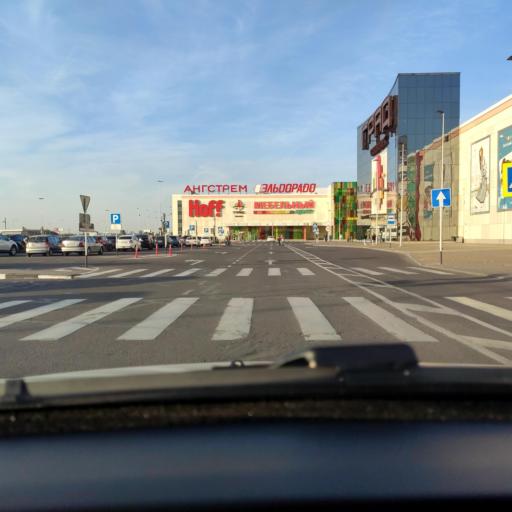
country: RU
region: Voronezj
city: Podgornoye
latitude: 51.7888
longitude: 39.2043
